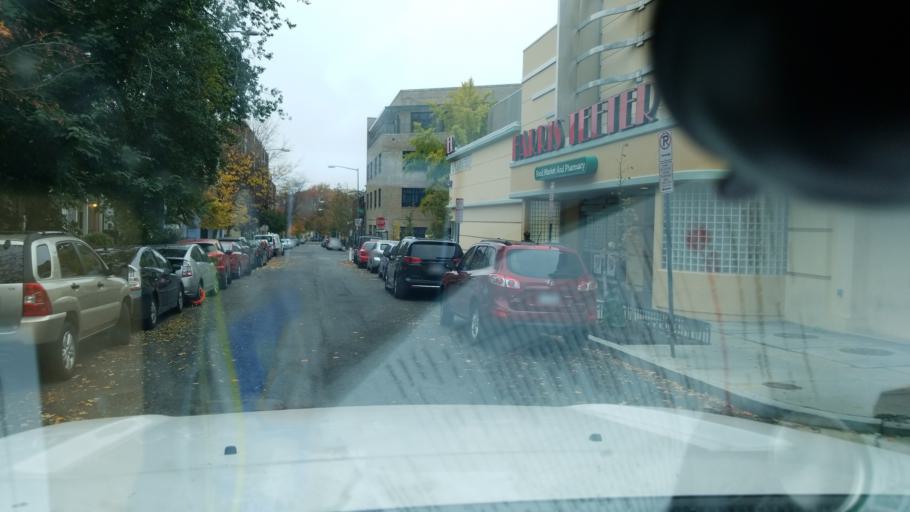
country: US
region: Washington, D.C.
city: Washington, D.C.
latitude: 38.9218
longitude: -77.0381
